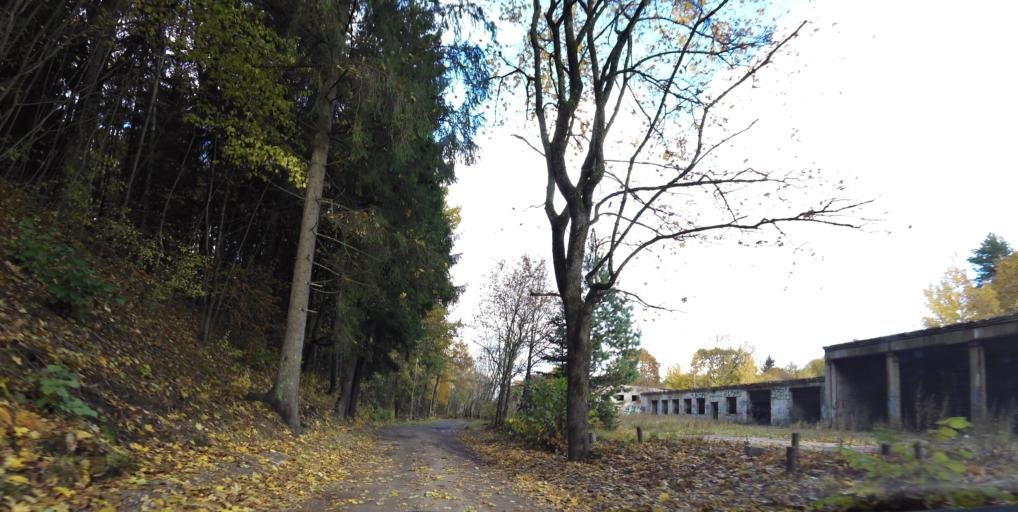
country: LT
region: Vilnius County
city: Vilkpede
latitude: 54.6561
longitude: 25.2579
